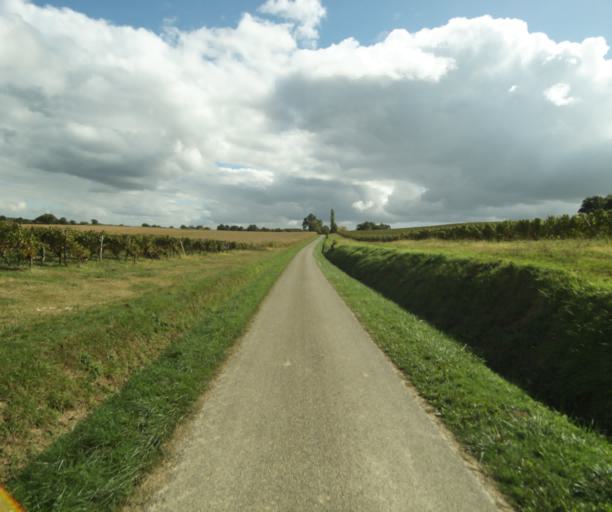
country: FR
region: Midi-Pyrenees
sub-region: Departement du Gers
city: Nogaro
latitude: 43.8479
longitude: -0.0313
